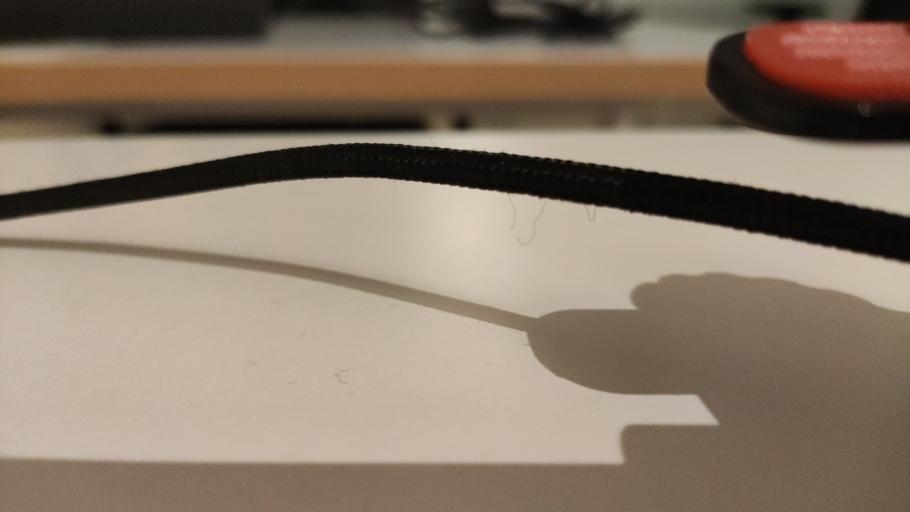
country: RU
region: Moskovskaya
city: Likino-Dulevo
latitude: 55.6989
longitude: 38.9559
